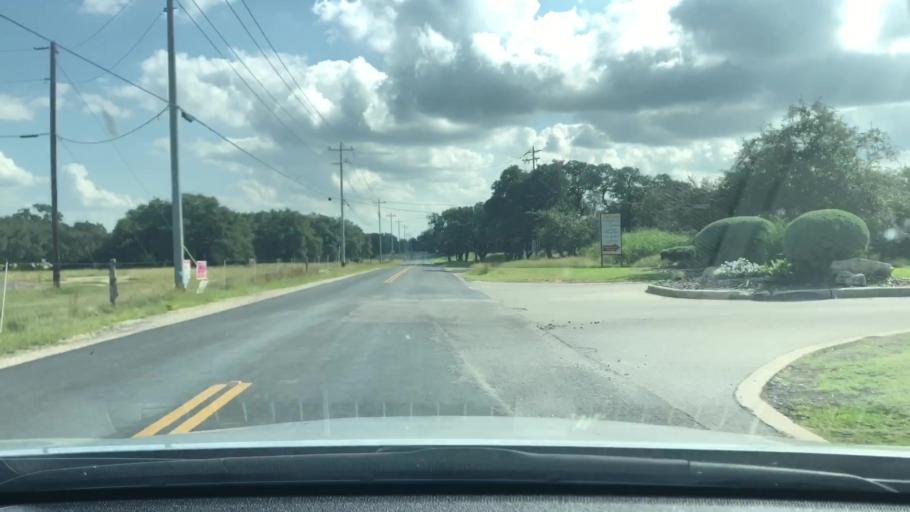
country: US
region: Texas
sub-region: Bexar County
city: Fair Oaks Ranch
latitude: 29.7759
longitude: -98.6264
